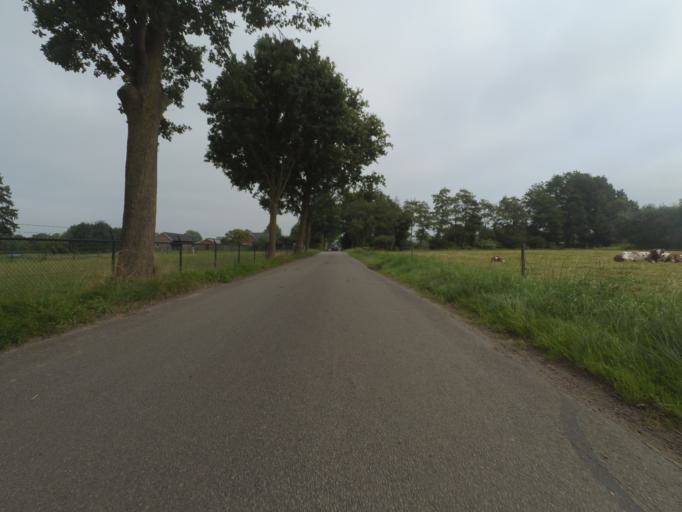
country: NL
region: Gelderland
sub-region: Gemeente Barneveld
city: Kootwijkerbroek
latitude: 52.1398
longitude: 5.6368
